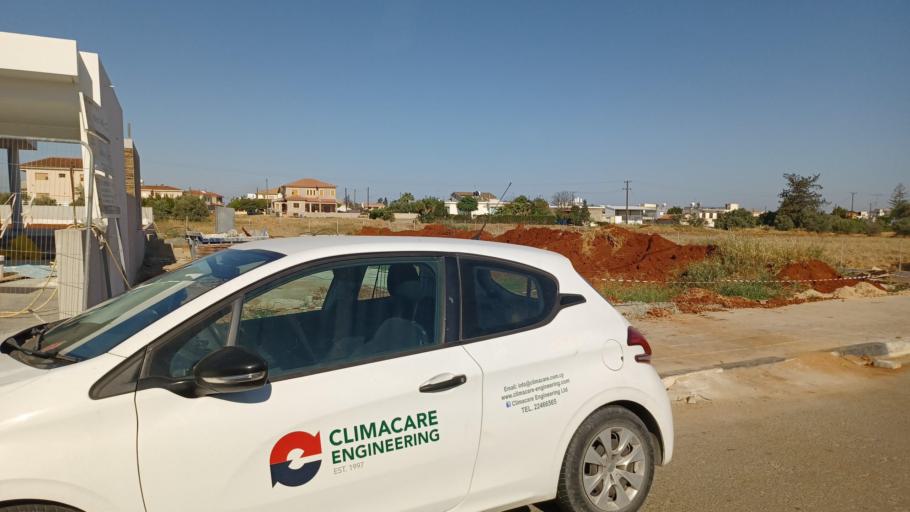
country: CY
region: Lefkosia
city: Kokkinotrimithia
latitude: 35.1466
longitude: 33.2080
